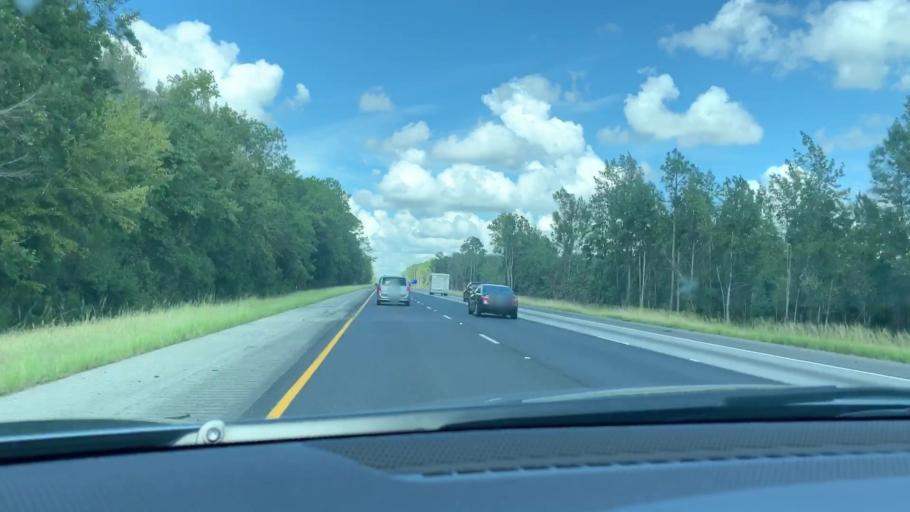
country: US
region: Georgia
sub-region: Camden County
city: Woodbine
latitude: 30.9162
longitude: -81.6859
